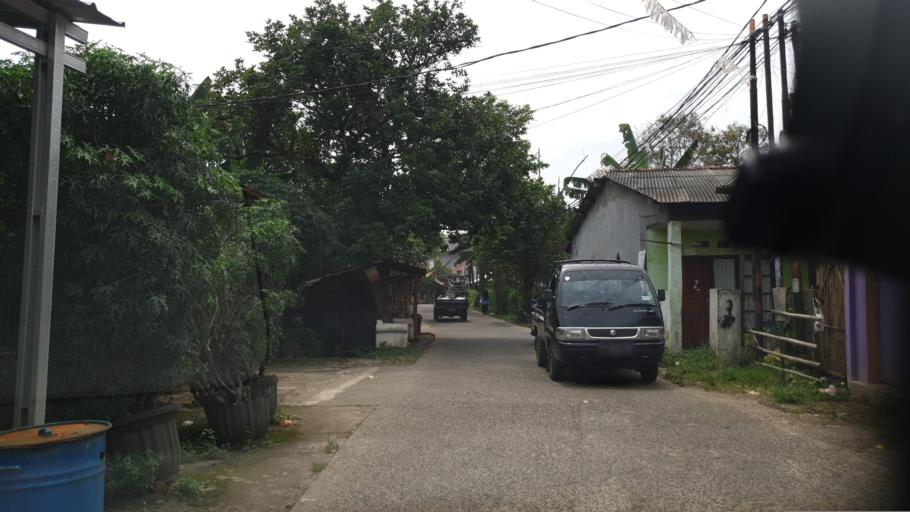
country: ID
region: West Java
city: Sawangan
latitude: -6.3788
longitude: 106.7603
